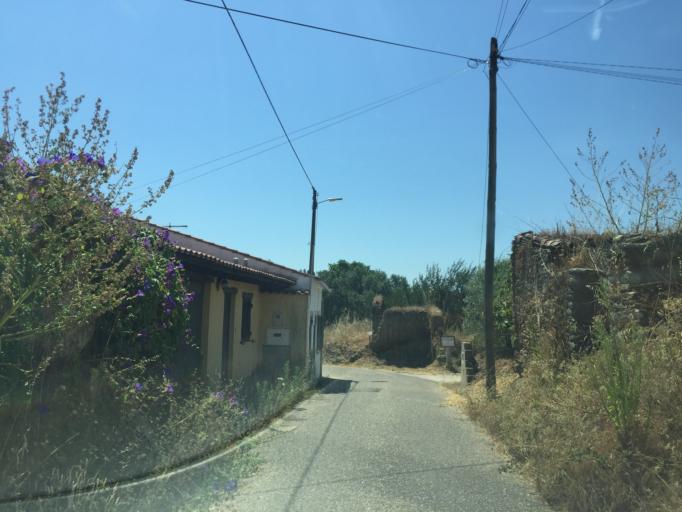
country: PT
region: Santarem
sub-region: Ferreira do Zezere
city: Ferreira do Zezere
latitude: 39.6261
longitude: -8.3192
